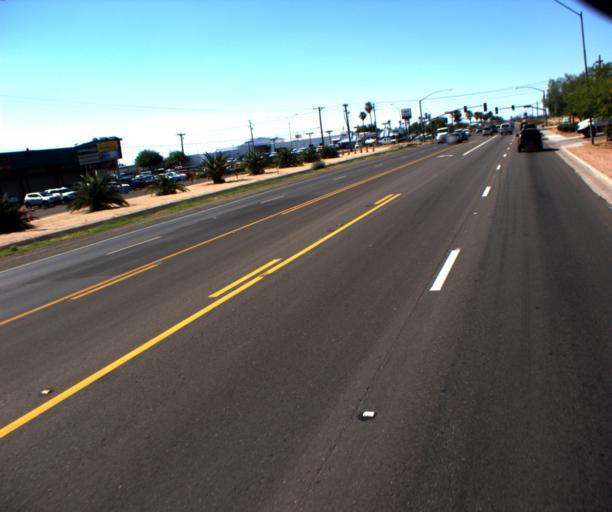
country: US
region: Arizona
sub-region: Pinal County
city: Casa Grande
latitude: 32.9101
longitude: -111.7573
